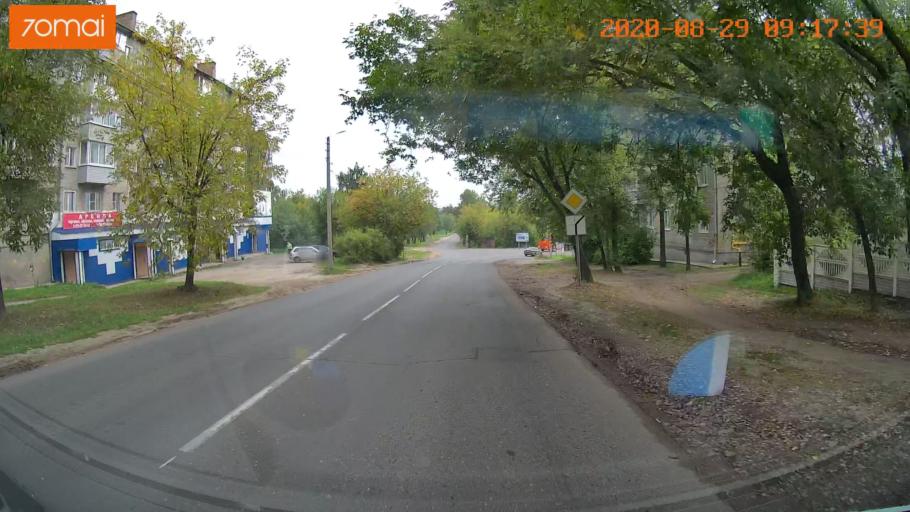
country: RU
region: Ivanovo
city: Kineshma
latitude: 57.4427
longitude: 42.1521
